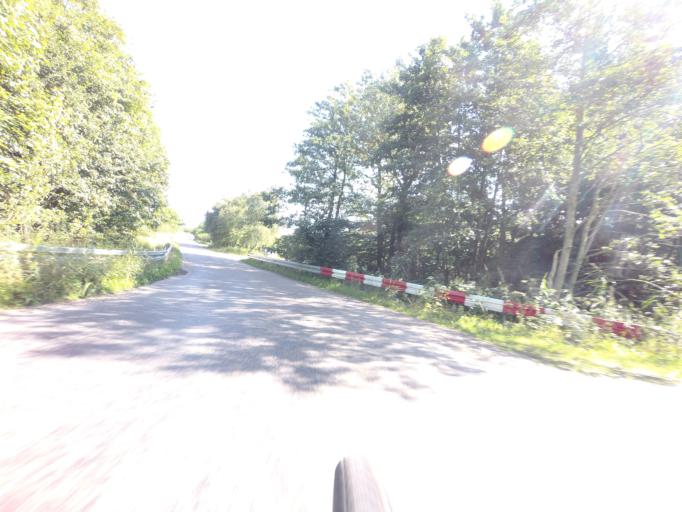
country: DK
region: North Denmark
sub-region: Hjorring Kommune
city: Hirtshals
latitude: 57.5788
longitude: 10.0069
